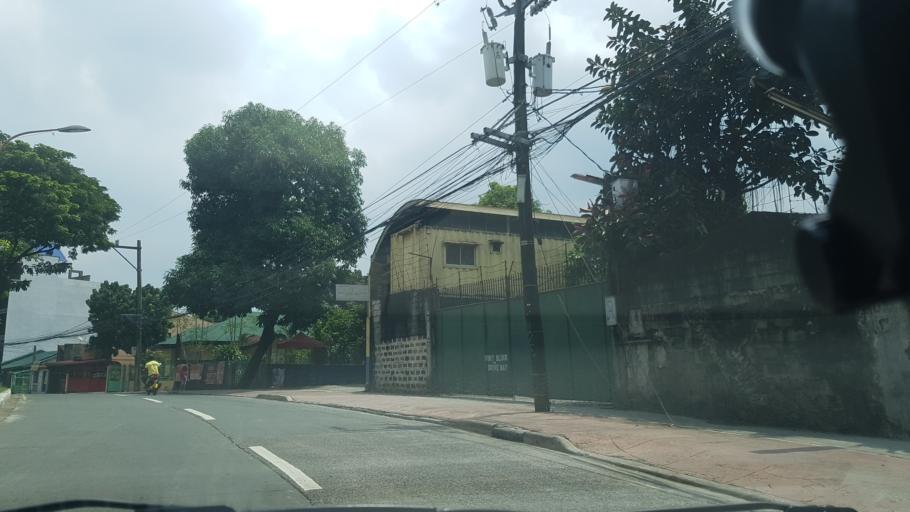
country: PH
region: Calabarzon
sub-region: Province of Rizal
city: Antipolo
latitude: 14.6481
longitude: 121.1152
